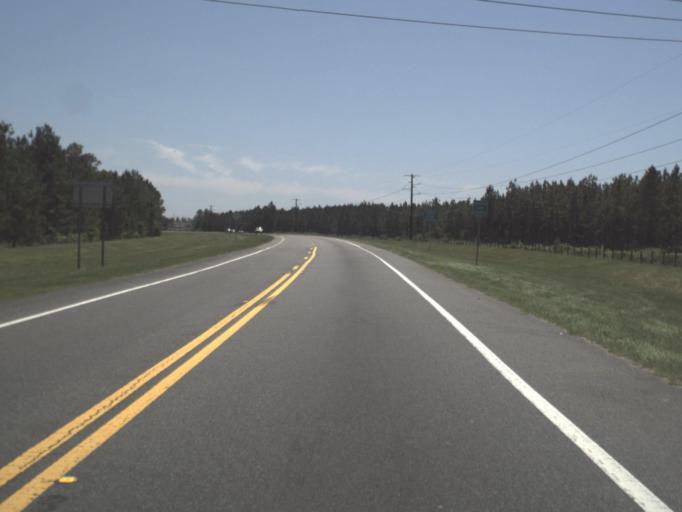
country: US
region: Florida
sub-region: Clay County
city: Lakeside
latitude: 30.1890
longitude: -81.8376
